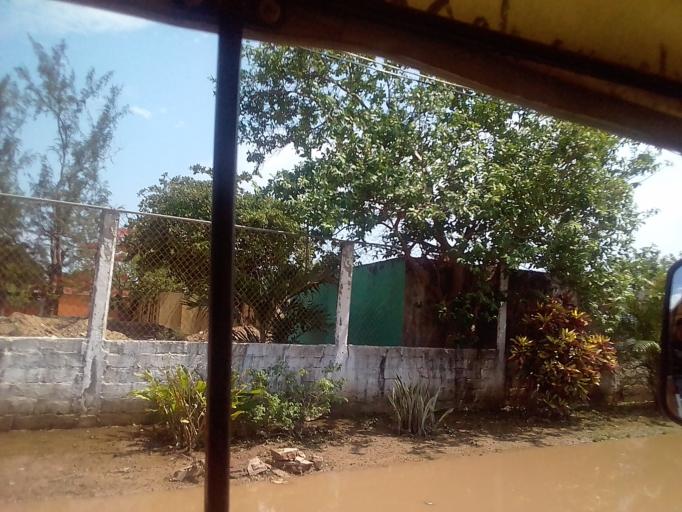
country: MX
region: Oaxaca
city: Union Hidalgo
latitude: 16.4655
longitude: -94.8308
